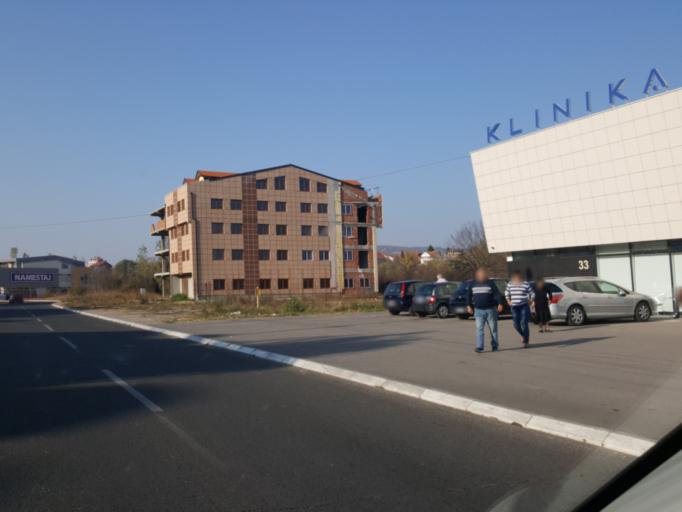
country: RS
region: Central Serbia
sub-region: Nisavski Okrug
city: Nis
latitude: 43.3228
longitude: 21.9323
